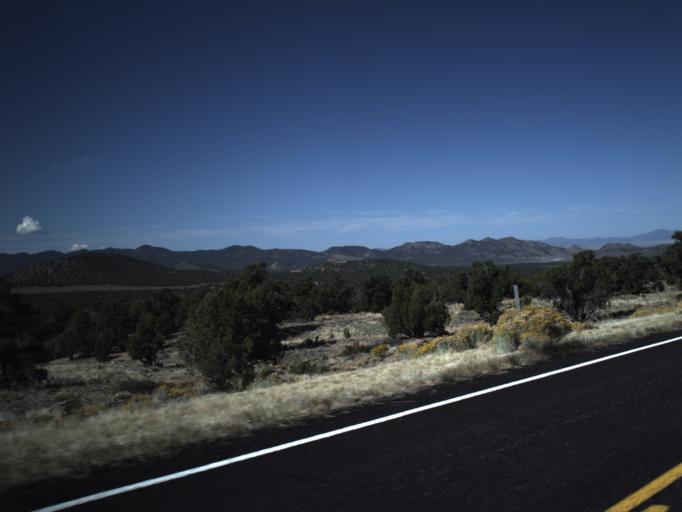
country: US
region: Utah
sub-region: Washington County
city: Enterprise
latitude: 37.6170
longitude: -113.4105
